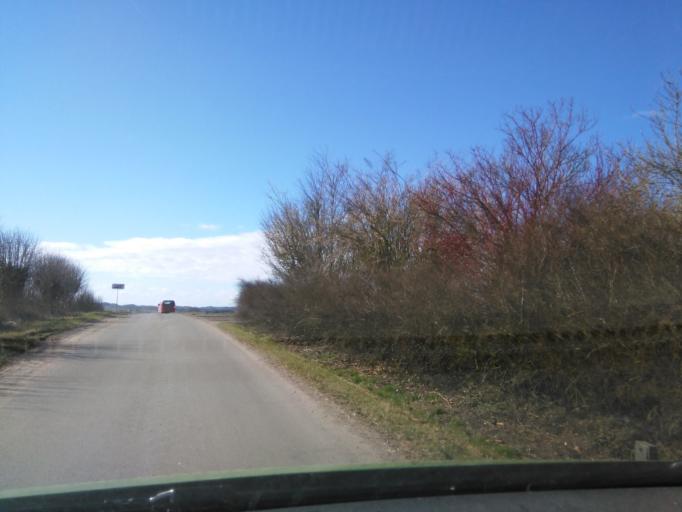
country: DK
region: Central Jutland
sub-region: Arhus Kommune
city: Solbjerg
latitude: 55.9796
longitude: 10.0434
